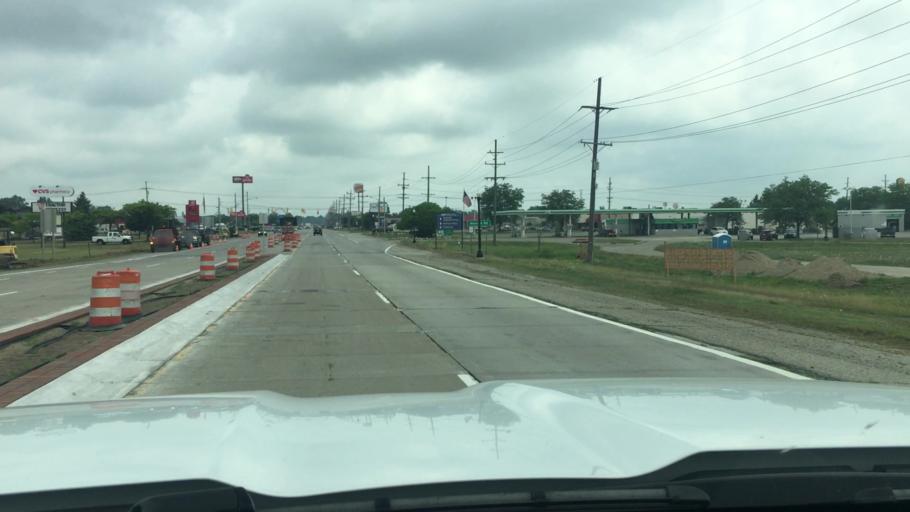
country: US
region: Michigan
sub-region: Lapeer County
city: Imlay City
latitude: 43.0049
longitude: -83.0714
